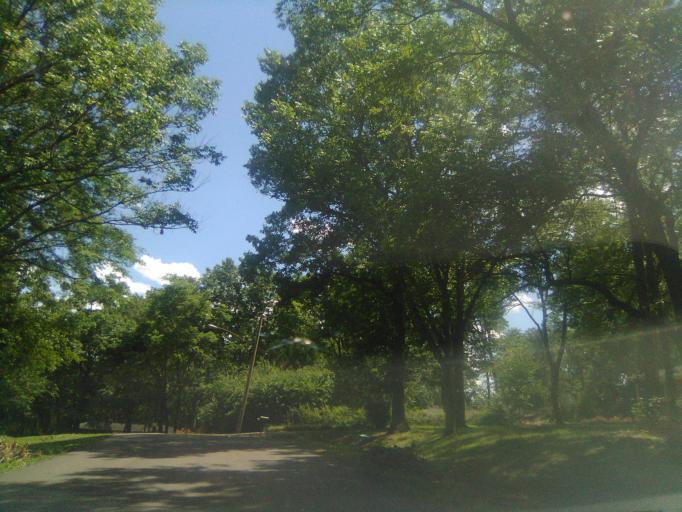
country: US
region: Tennessee
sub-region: Davidson County
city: Belle Meade
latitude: 36.1296
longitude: -86.8613
